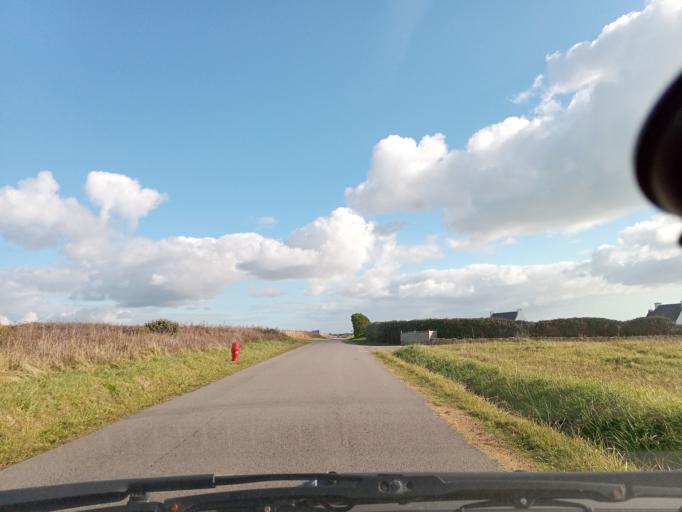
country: FR
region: Brittany
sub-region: Departement du Finistere
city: Plozevet
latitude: 47.9753
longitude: -4.4426
